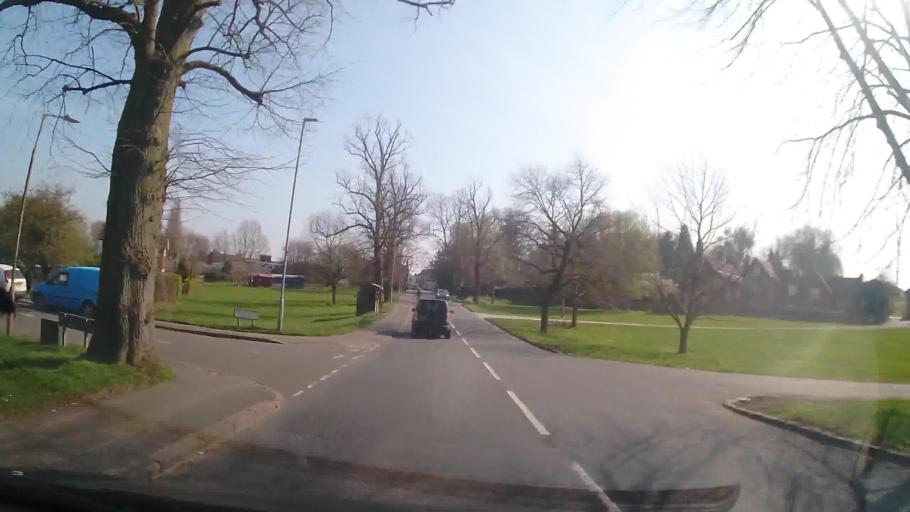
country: GB
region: England
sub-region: Leicestershire
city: Anstey
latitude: 52.6734
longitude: -1.1956
